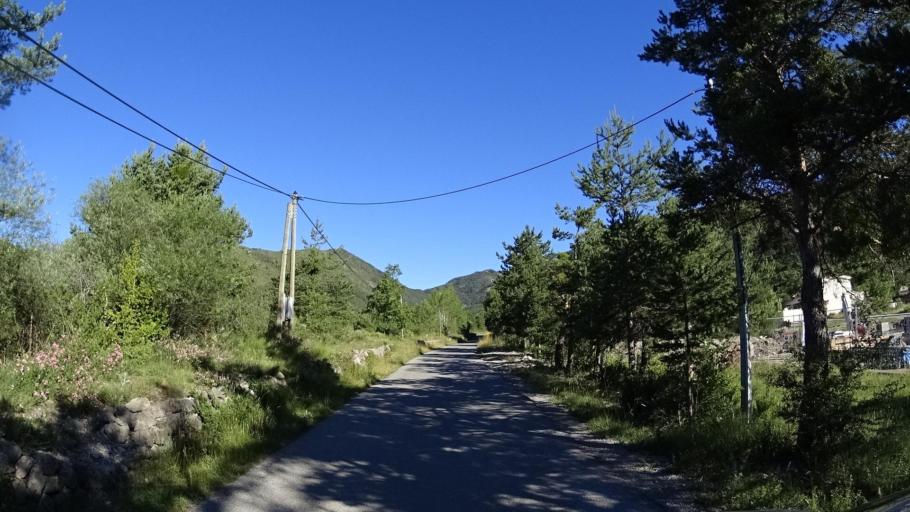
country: FR
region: Provence-Alpes-Cote d'Azur
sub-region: Departement des Alpes-de-Haute-Provence
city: Castellane
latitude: 43.8768
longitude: 6.5064
